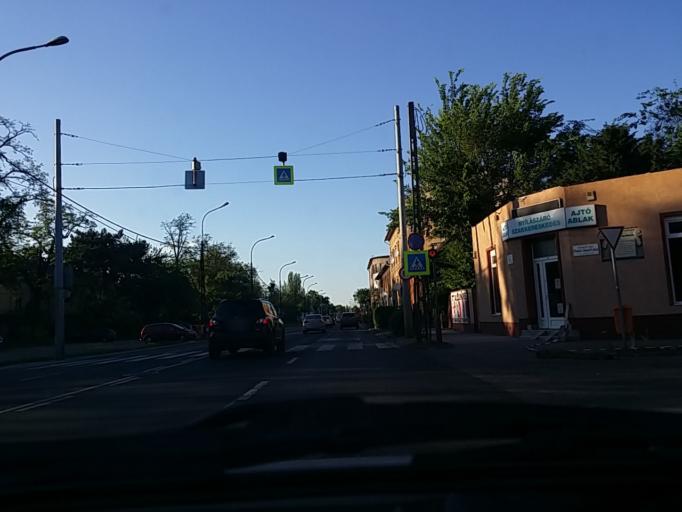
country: HU
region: Budapest
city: Budapest IV. keruelet
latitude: 47.5798
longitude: 19.0815
